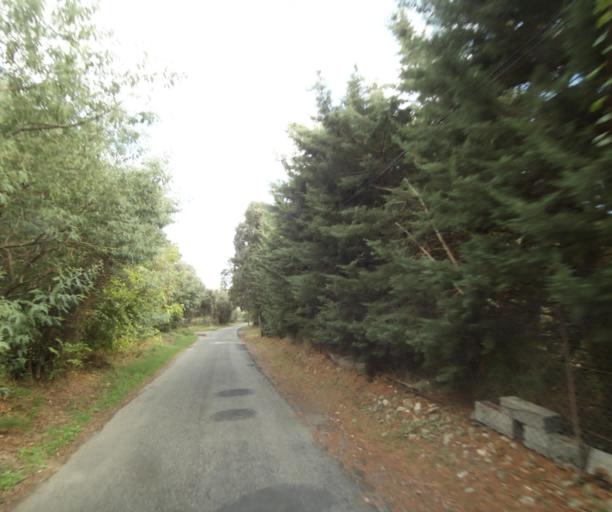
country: FR
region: Languedoc-Roussillon
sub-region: Departement des Pyrenees-Orientales
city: Argelers
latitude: 42.5450
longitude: 3.0009
